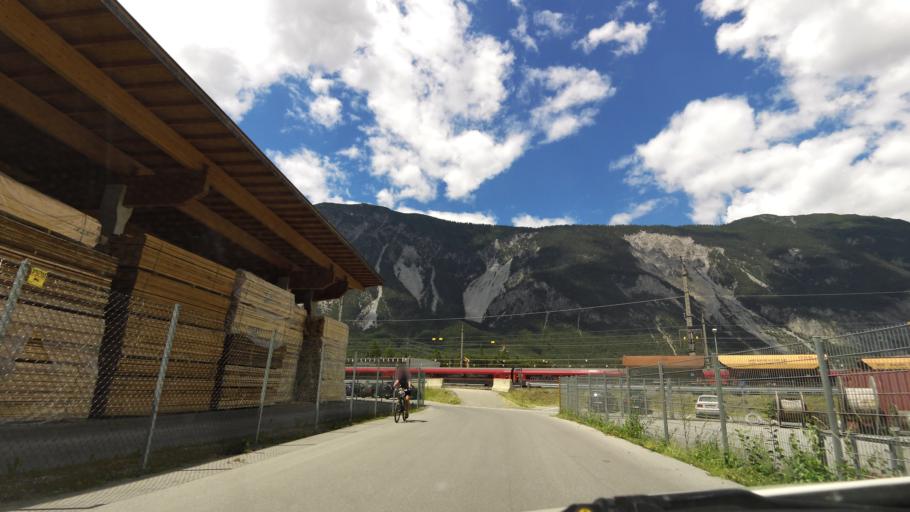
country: AT
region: Tyrol
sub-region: Politischer Bezirk Imst
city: Haiming
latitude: 47.2379
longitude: 10.8629
